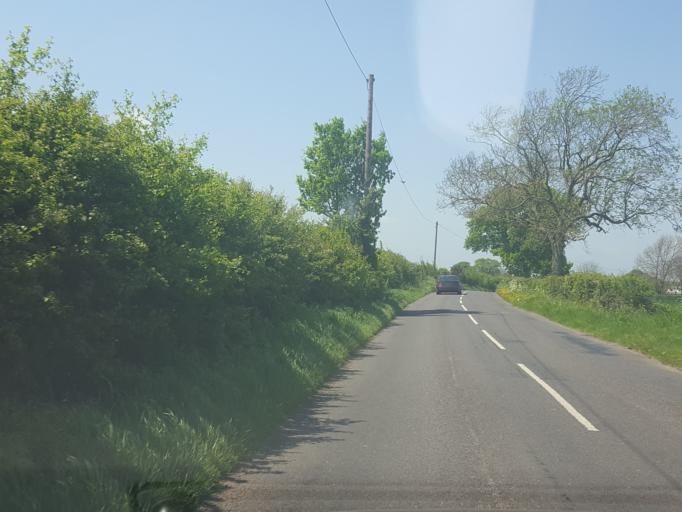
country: GB
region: England
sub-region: Essex
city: Great Bentley
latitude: 51.8546
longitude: 1.0816
